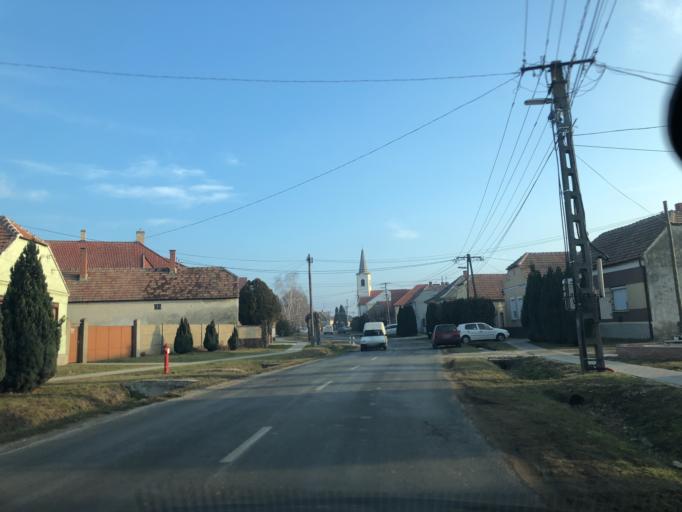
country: HU
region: Gyor-Moson-Sopron
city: Kapuvar
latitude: 47.5999
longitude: 17.0860
